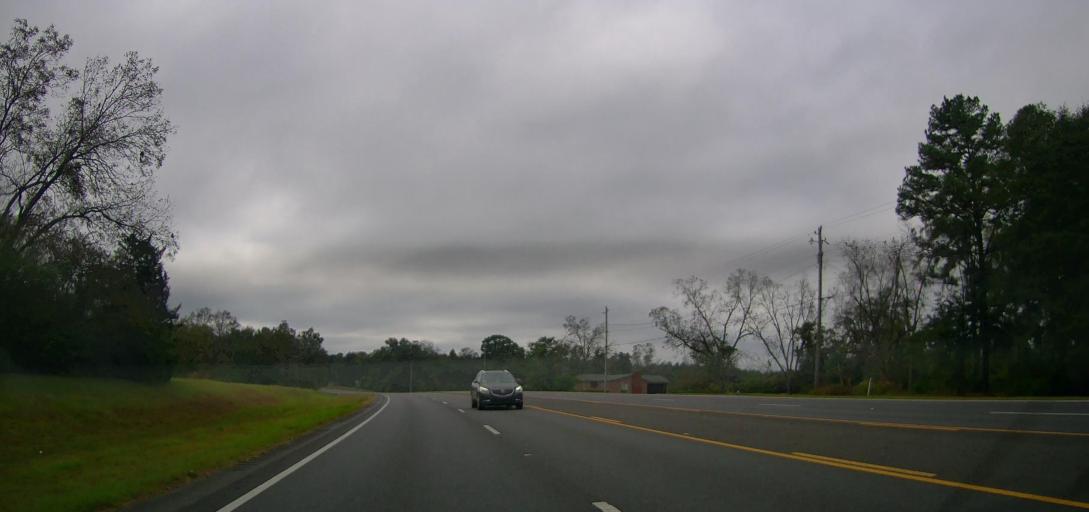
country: US
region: Georgia
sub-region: Thomas County
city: Thomasville
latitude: 30.9412
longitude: -83.9080
